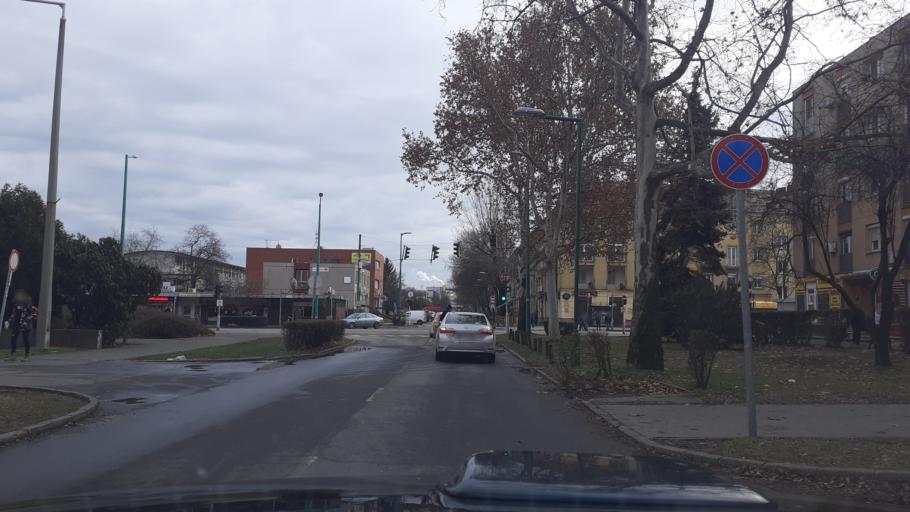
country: HU
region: Fejer
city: dunaujvaros
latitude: 46.9626
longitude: 18.9332
